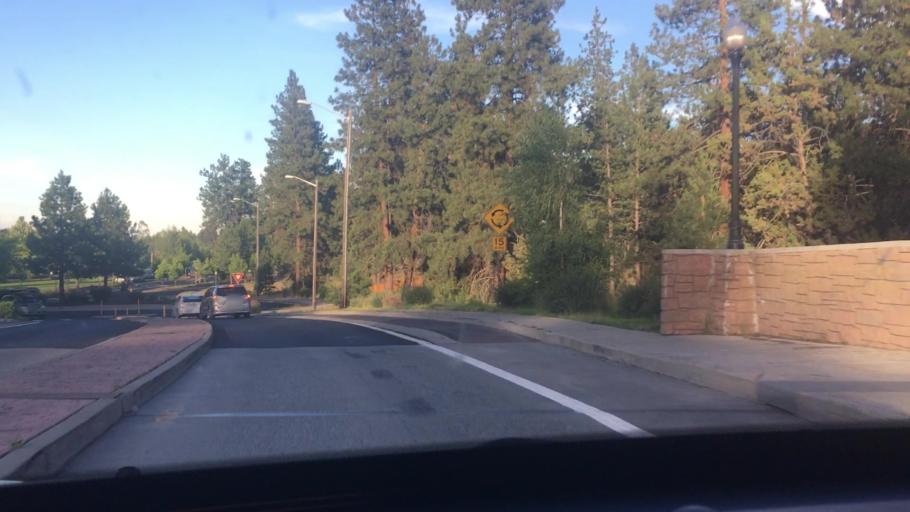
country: US
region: Oregon
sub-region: Deschutes County
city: Bend
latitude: 44.0406
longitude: -121.3292
